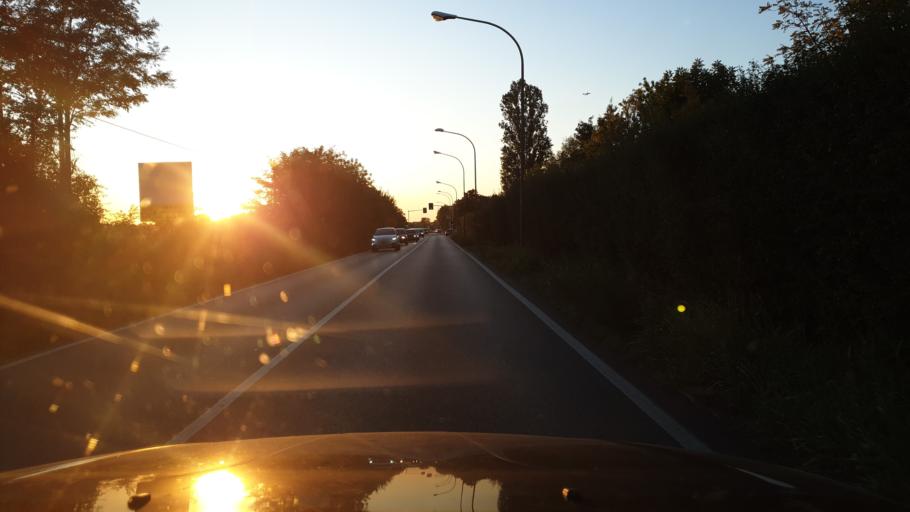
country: IT
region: Emilia-Romagna
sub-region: Provincia di Bologna
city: Quarto Inferiore
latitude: 44.5285
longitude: 11.3858
